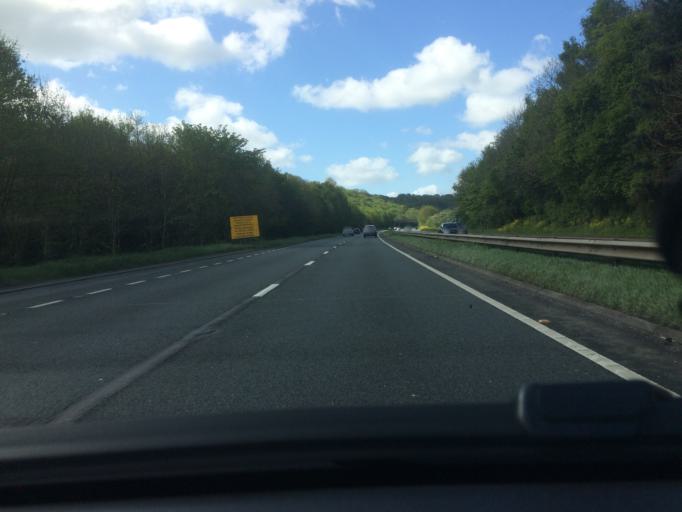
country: GB
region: Wales
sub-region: Wrexham
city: Gresford
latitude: 53.0982
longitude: -2.9646
